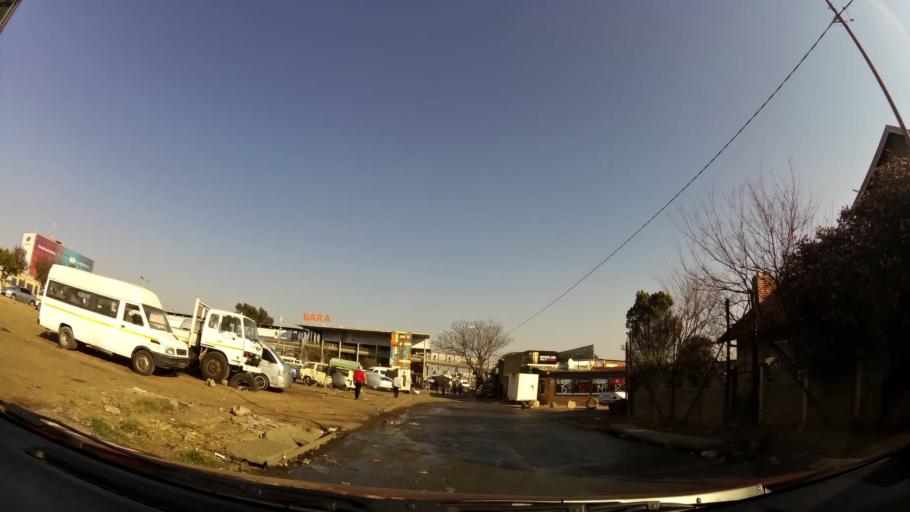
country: ZA
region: Gauteng
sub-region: City of Johannesburg Metropolitan Municipality
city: Soweto
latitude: -26.2595
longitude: 27.9447
